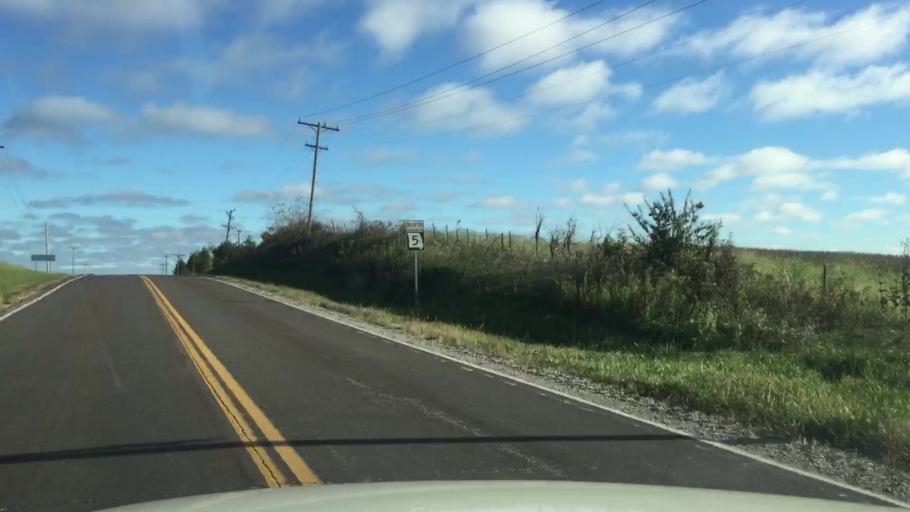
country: US
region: Missouri
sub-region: Howard County
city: Fayette
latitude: 39.1045
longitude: -92.7339
